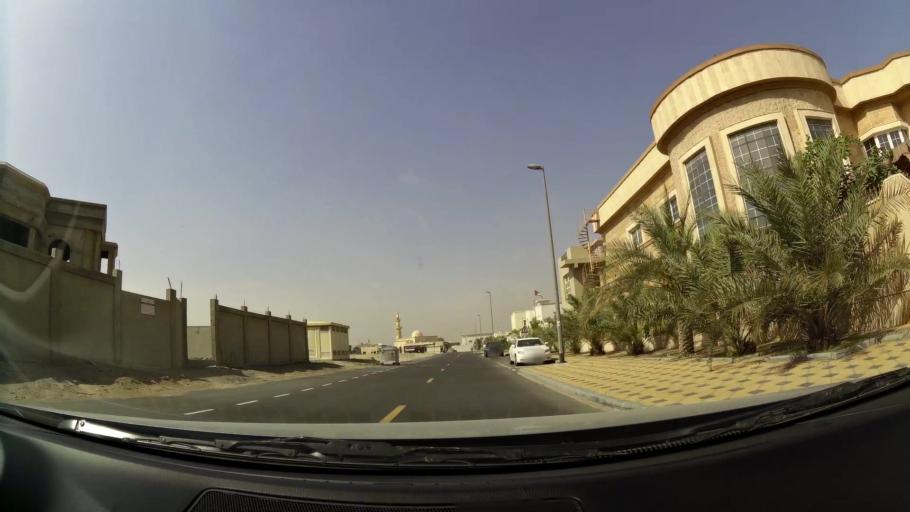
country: AE
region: Ash Shariqah
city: Sharjah
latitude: 25.2073
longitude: 55.4168
